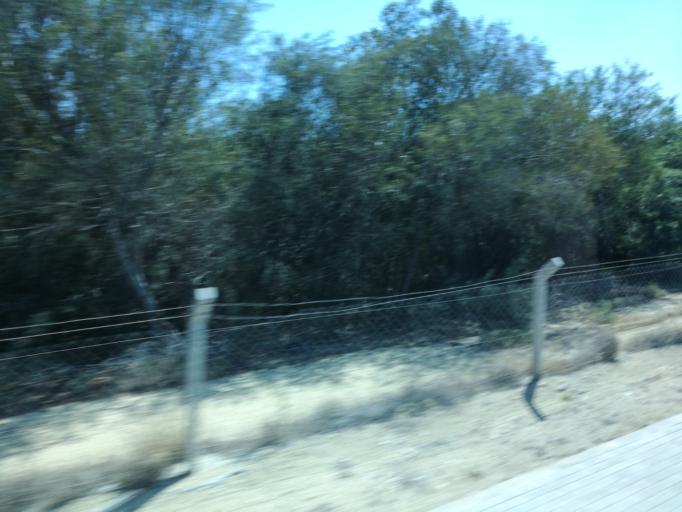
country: CY
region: Ammochostos
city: Famagusta
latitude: 35.1518
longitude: 33.9069
